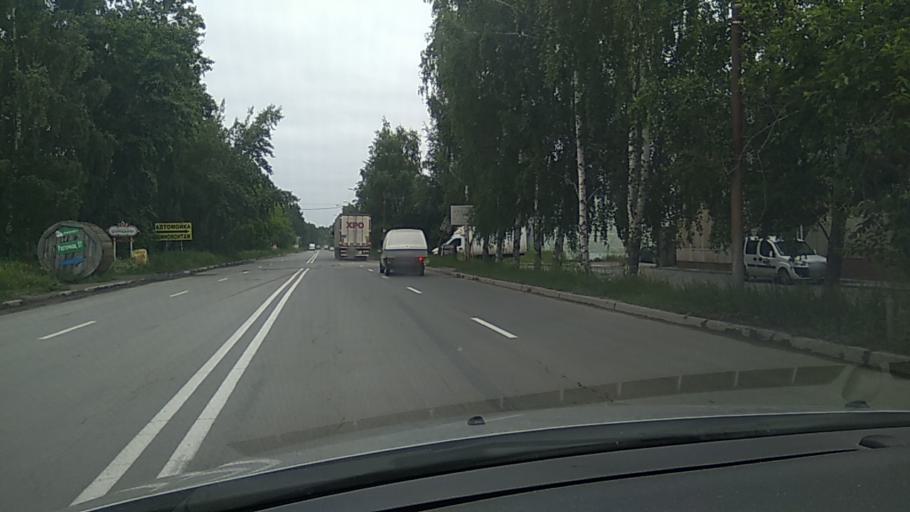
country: RU
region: Sverdlovsk
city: Shuvakish
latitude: 56.8891
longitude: 60.5232
